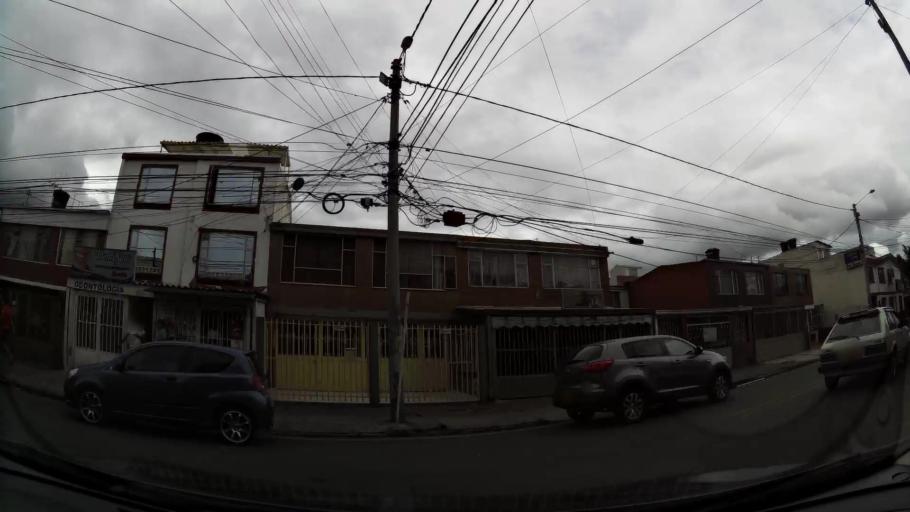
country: CO
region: Bogota D.C.
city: Barrio San Luis
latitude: 4.6881
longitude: -74.0910
